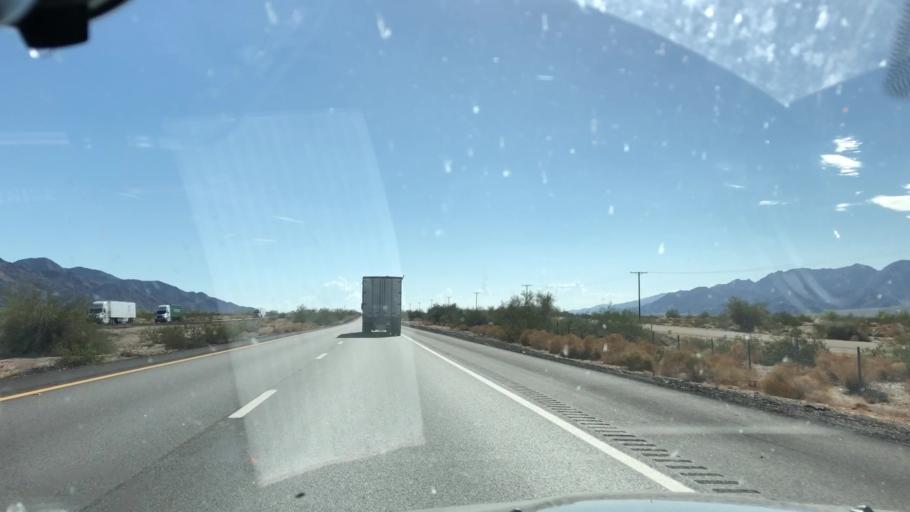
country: US
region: California
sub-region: Imperial County
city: Niland
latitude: 33.7090
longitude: -115.4223
